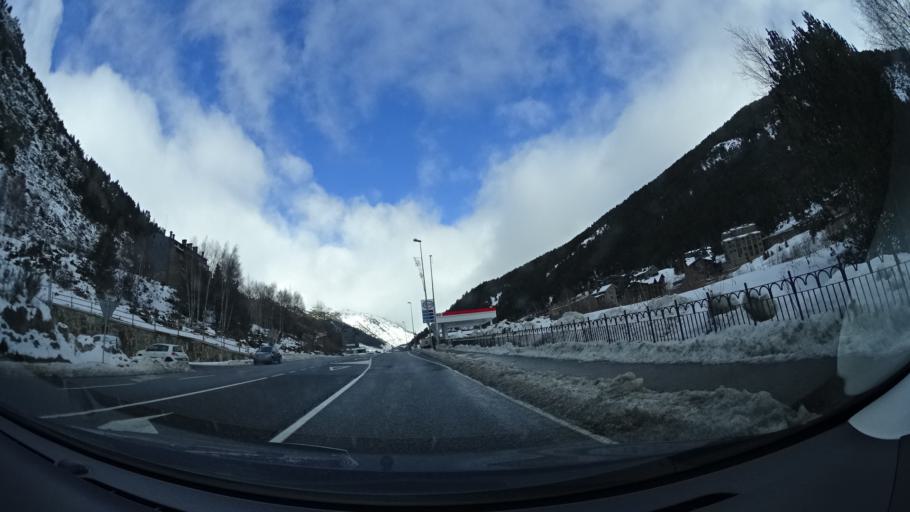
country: AD
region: Canillo
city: El Tarter
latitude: 42.5809
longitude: 1.6607
